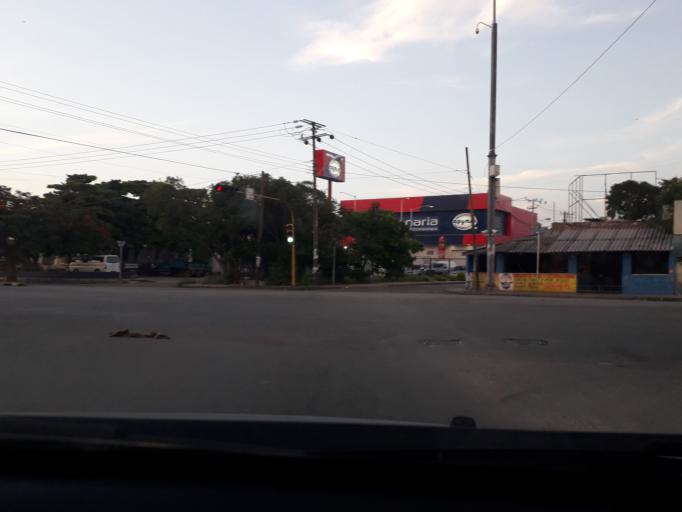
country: MX
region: Yucatan
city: Merida
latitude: 20.9839
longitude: -89.6547
